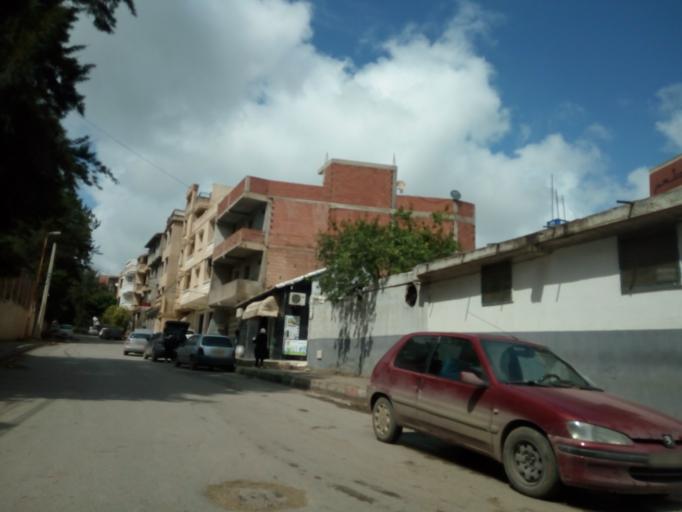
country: DZ
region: Tipaza
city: Douera
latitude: 36.6988
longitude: 2.9776
